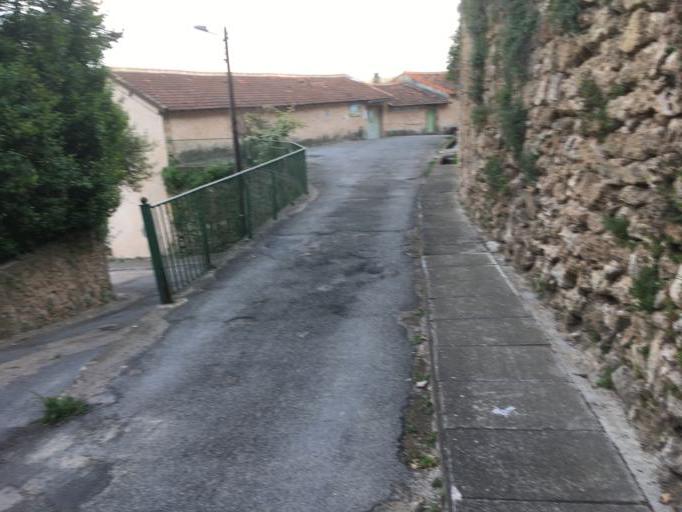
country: FR
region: Provence-Alpes-Cote d'Azur
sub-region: Departement du Var
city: Salernes
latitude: 43.5662
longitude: 6.2323
